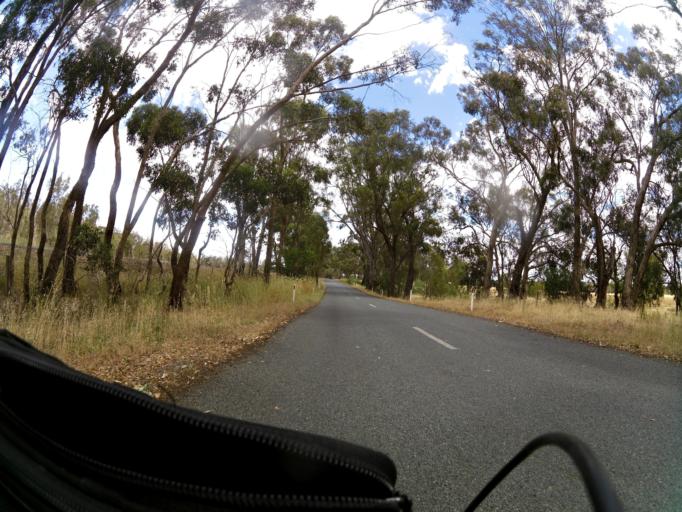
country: AU
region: Victoria
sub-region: Greater Shepparton
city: Shepparton
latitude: -36.6493
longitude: 145.2080
